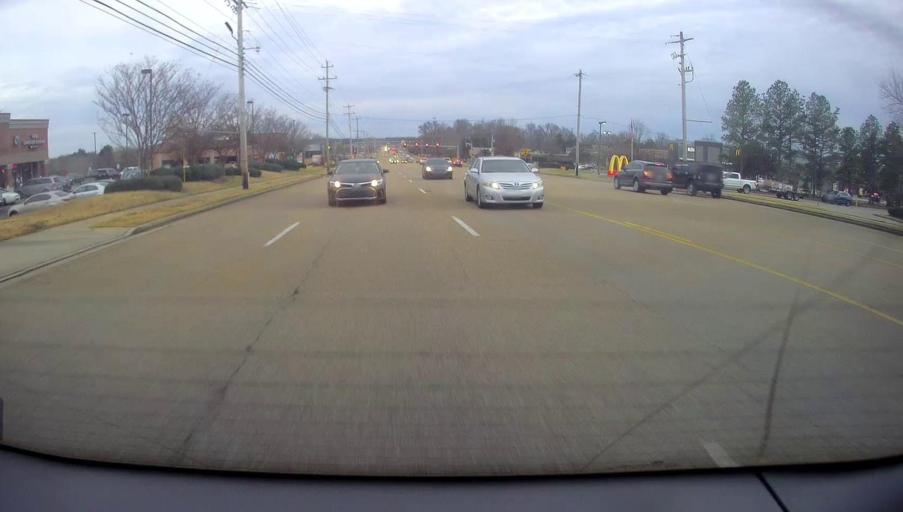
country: US
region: Tennessee
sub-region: Shelby County
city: Germantown
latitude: 35.0455
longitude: -89.7959
